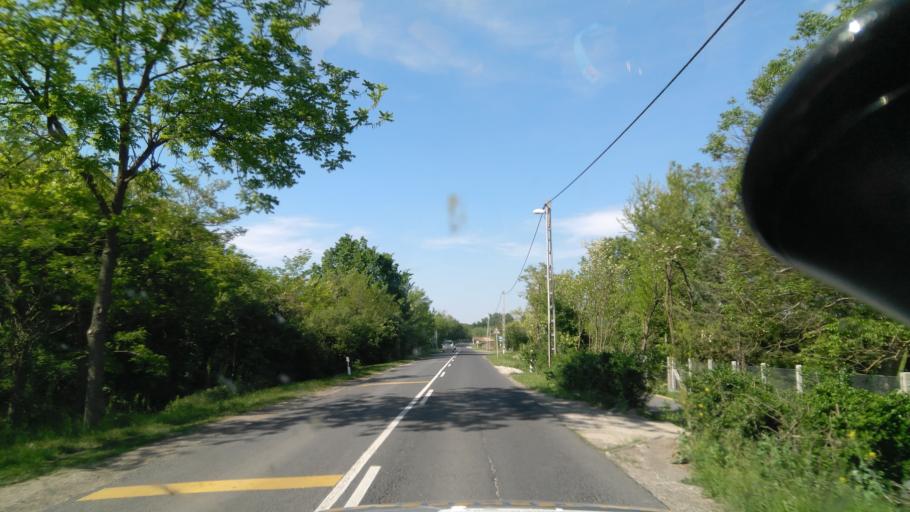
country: HU
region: Bekes
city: Gyula
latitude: 46.6968
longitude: 21.3105
